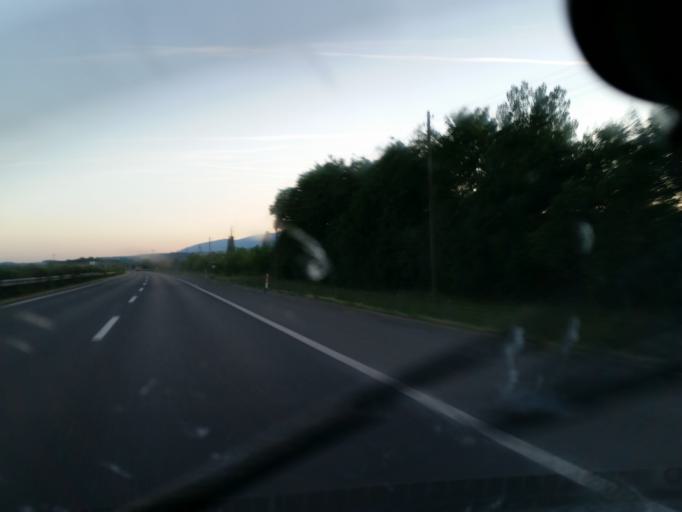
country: CH
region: Vaud
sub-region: Jura-Nord vaudois District
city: Chavornay
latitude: 46.7355
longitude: 6.5777
